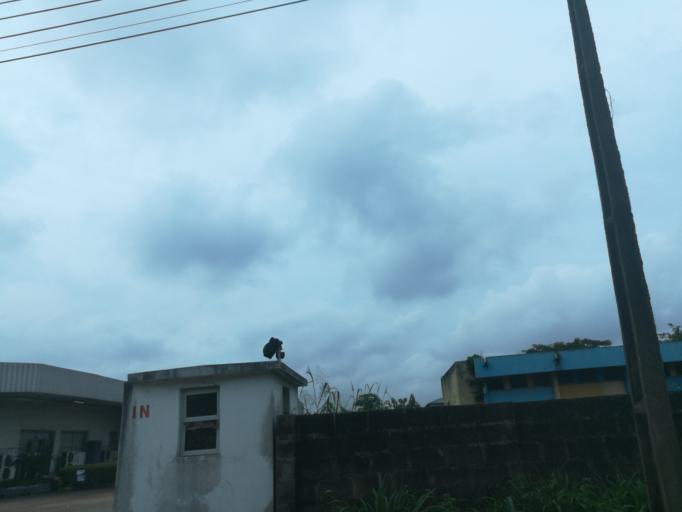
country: NG
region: Lagos
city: Oshodi
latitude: 6.5675
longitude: 3.3591
